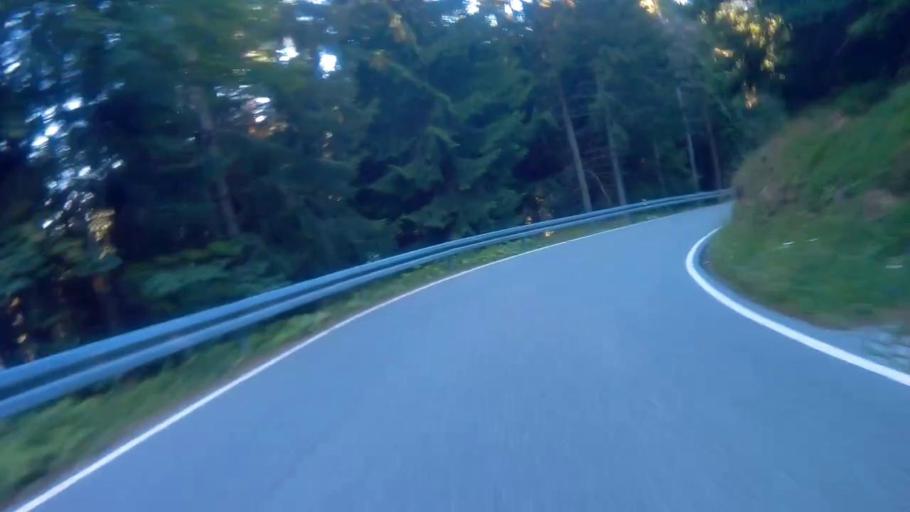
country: DE
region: Baden-Wuerttemberg
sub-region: Freiburg Region
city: Horben
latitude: 47.8916
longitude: 7.8707
